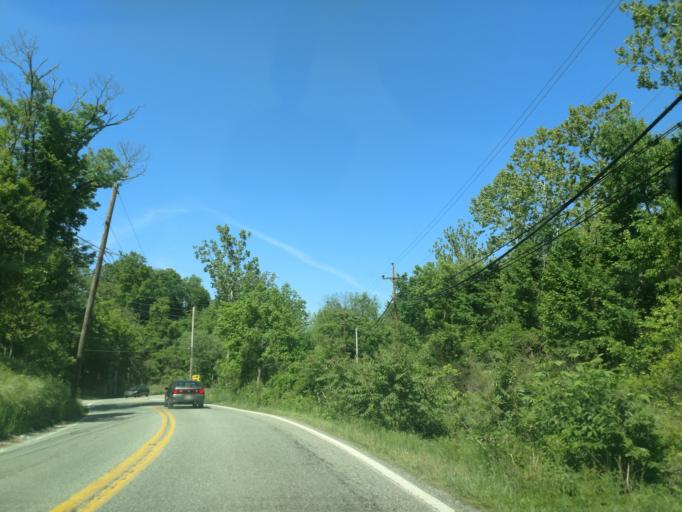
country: US
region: Pennsylvania
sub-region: Montgomery County
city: King of Prussia
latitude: 40.1054
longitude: -75.4084
